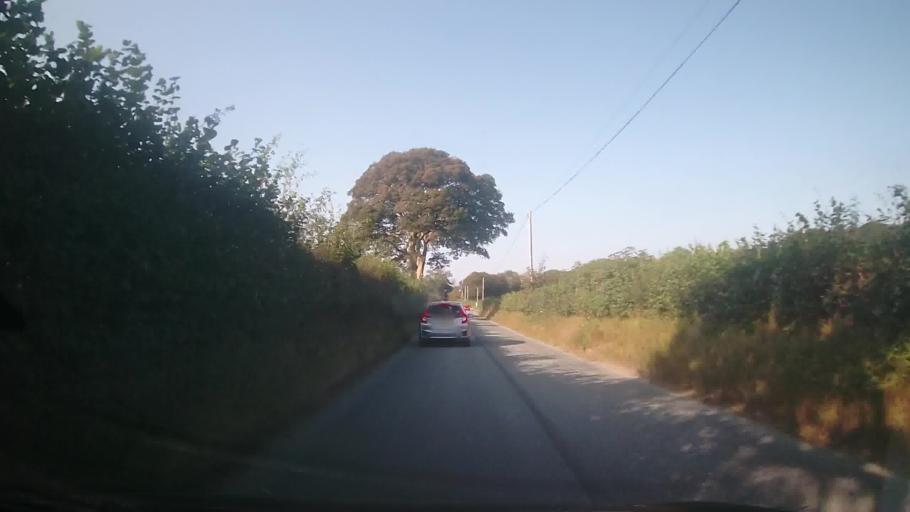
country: GB
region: Wales
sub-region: County of Ceredigion
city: Lledrod
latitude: 52.2254
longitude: -3.9320
